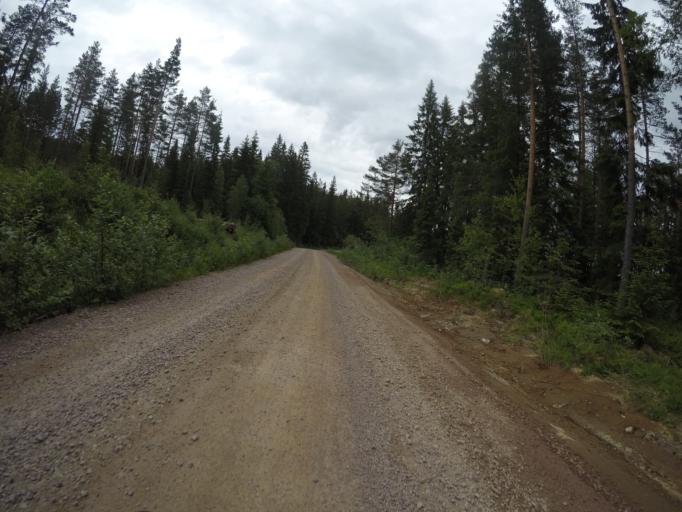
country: SE
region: Dalarna
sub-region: Ludvika Kommun
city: Abborrberget
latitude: 60.1034
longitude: 14.5255
